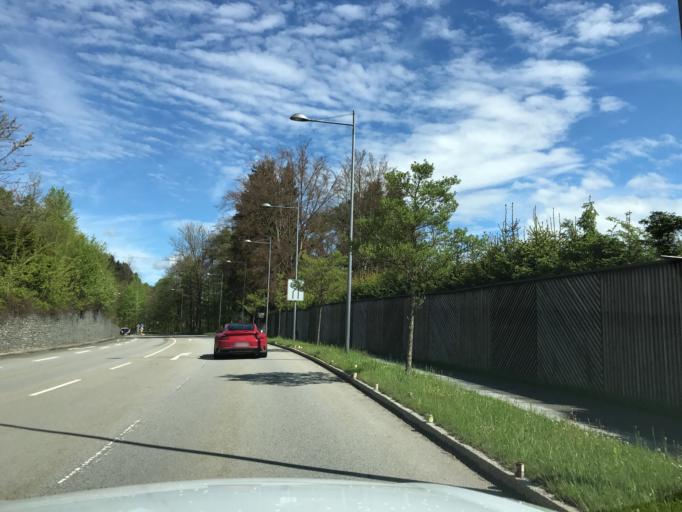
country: DE
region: Bavaria
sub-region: Upper Bavaria
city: Bad Wiessee
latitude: 47.7262
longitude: 11.7179
